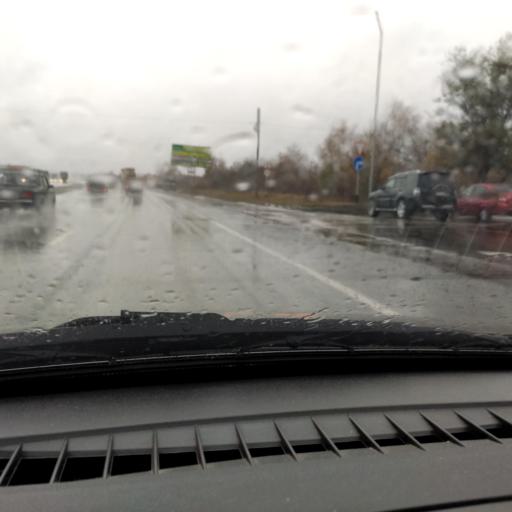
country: RU
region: Samara
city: Tol'yatti
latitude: 53.5779
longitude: 49.4010
